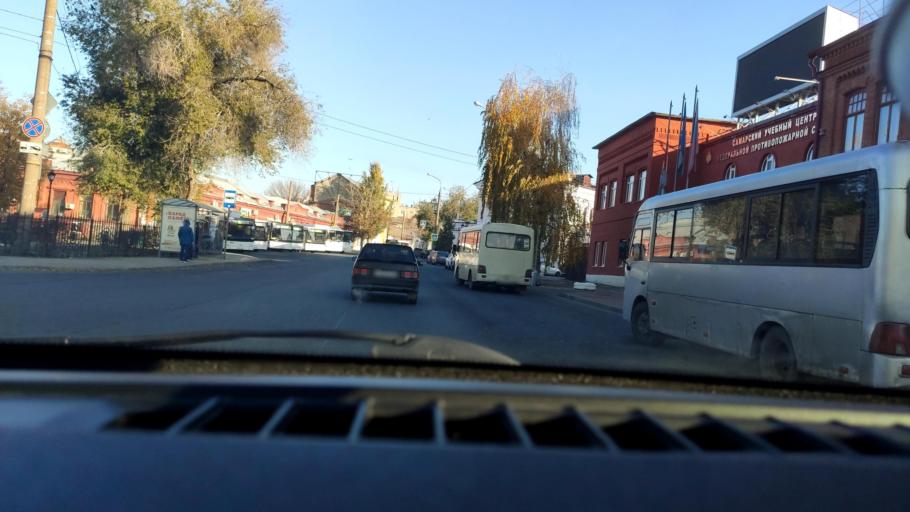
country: RU
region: Samara
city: Rozhdestveno
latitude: 53.1793
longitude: 50.0796
